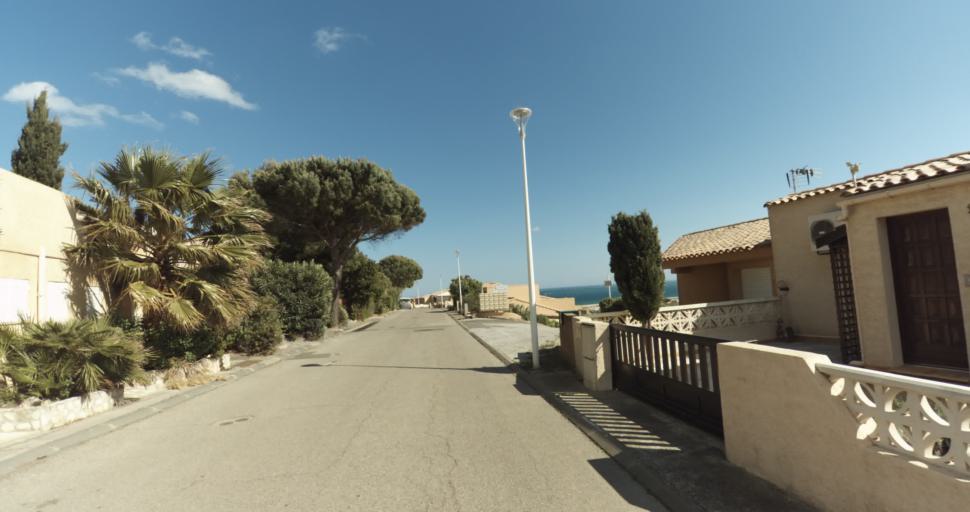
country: FR
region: Languedoc-Roussillon
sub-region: Departement de l'Aude
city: Leucate
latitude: 42.9051
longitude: 3.0480
